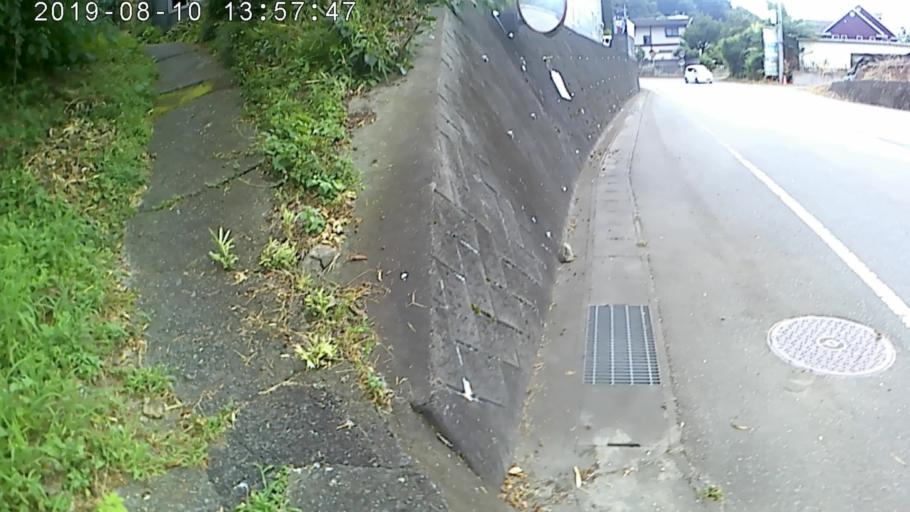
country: JP
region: Yamanashi
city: Uenohara
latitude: 35.6325
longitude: 139.1051
